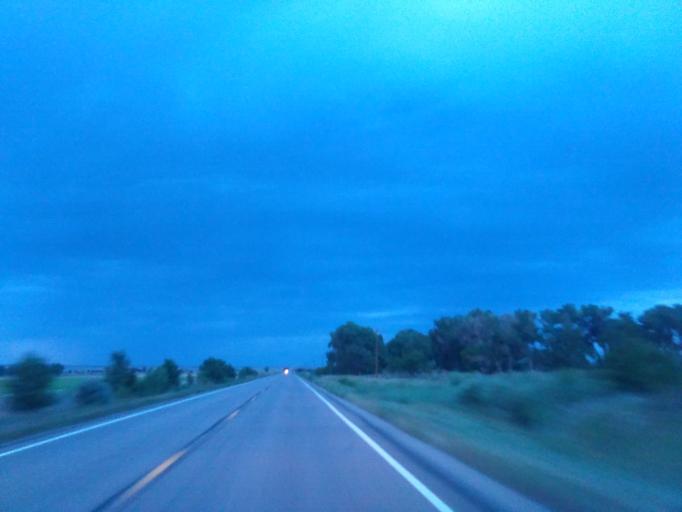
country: US
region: Colorado
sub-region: Las Animas County
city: Trinidad
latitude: 37.2657
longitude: -104.3537
